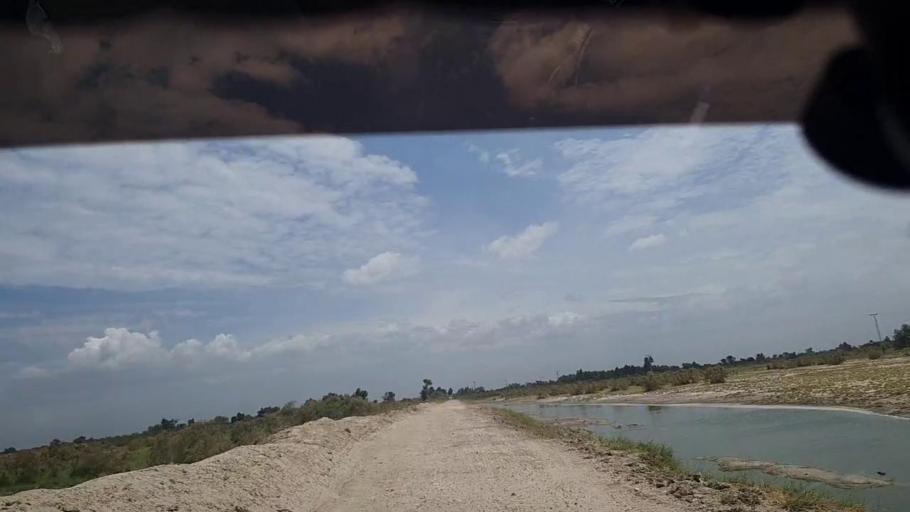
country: PK
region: Sindh
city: Rustam jo Goth
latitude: 28.0279
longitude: 68.9365
